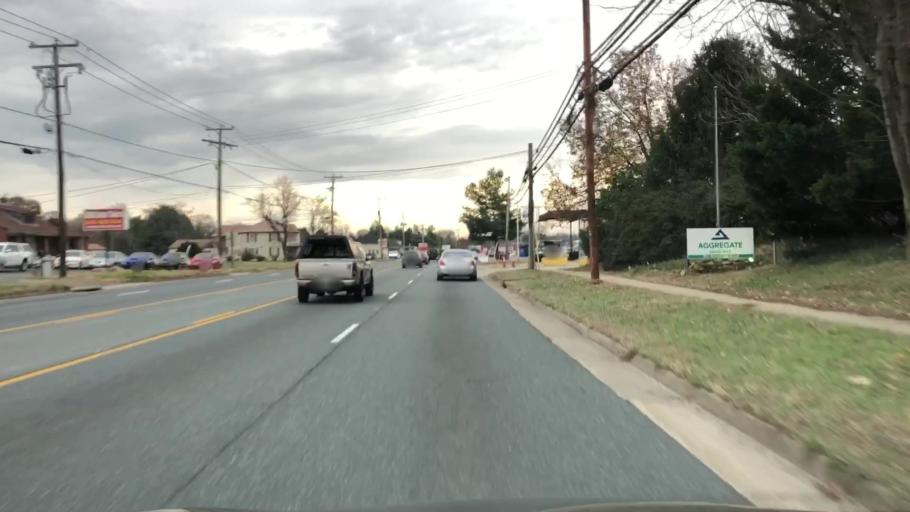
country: US
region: Virginia
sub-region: Stafford County
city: Falmouth
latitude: 38.3362
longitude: -77.4836
